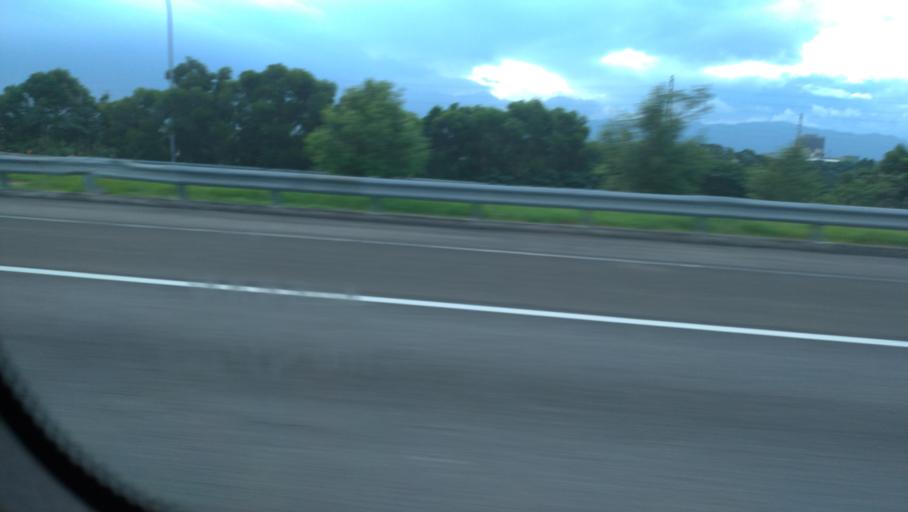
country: TW
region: Taiwan
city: Daxi
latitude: 24.8931
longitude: 121.2650
